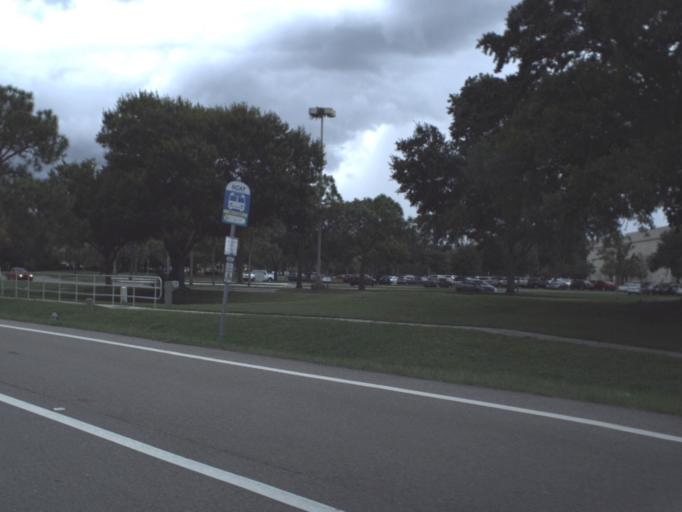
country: US
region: Florida
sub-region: Sarasota County
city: Vamo
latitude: 27.2322
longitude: -82.4964
